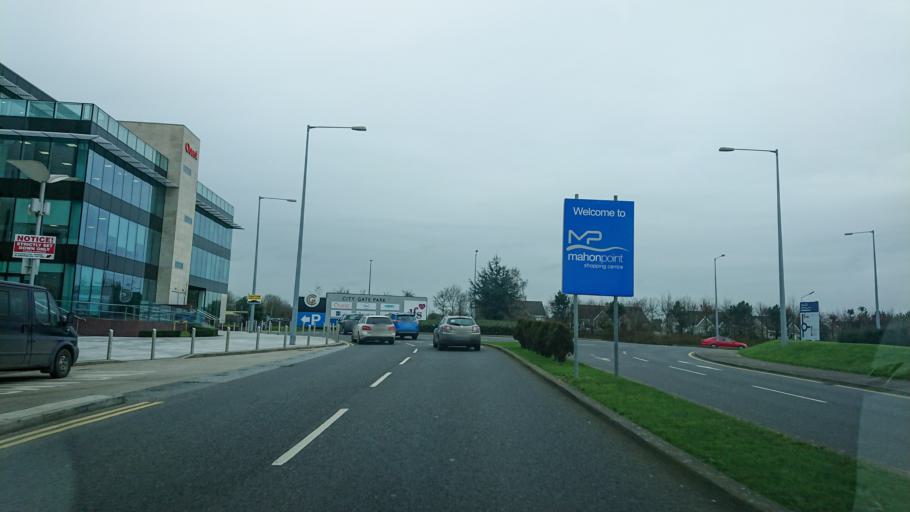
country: IE
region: Munster
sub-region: County Cork
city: Passage West
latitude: 51.8865
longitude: -8.4014
